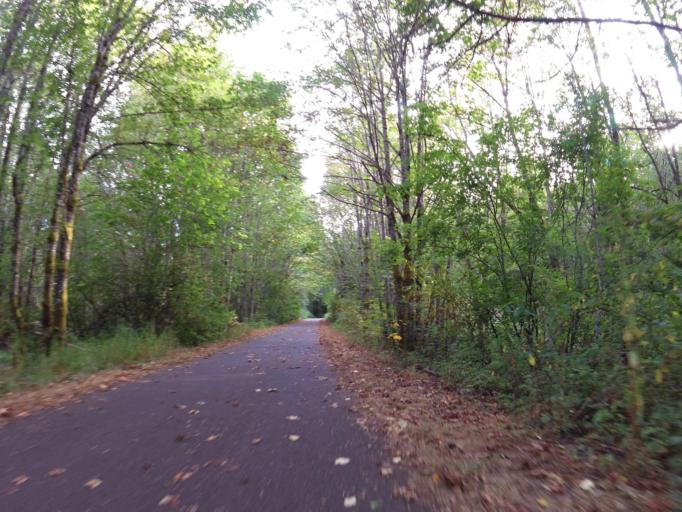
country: US
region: Washington
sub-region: Thurston County
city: Lacey
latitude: 46.9491
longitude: -122.8147
